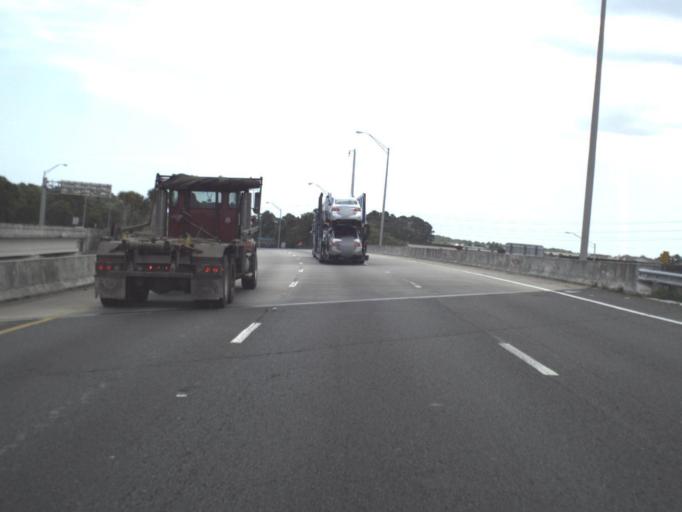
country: US
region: Florida
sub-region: Duval County
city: Jacksonville
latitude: 30.3492
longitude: -81.5530
